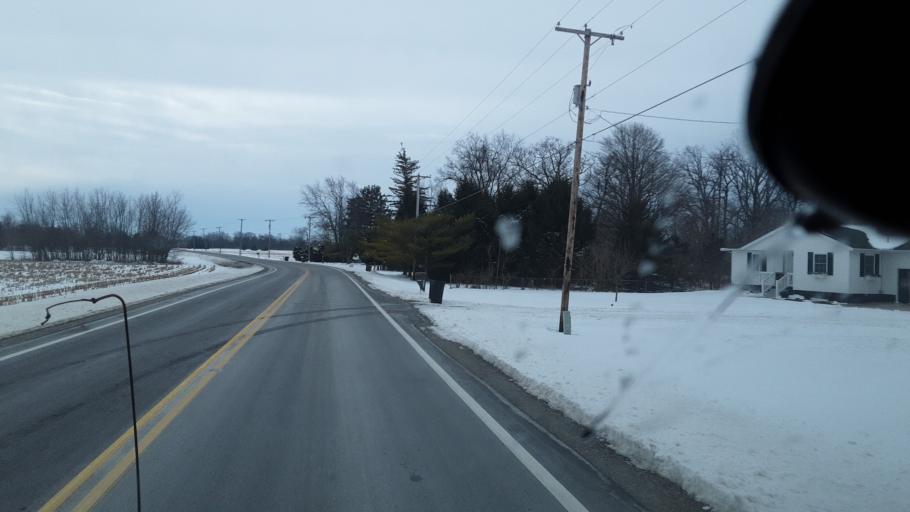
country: US
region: Ohio
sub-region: Madison County
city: London
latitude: 39.8479
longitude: -83.4665
